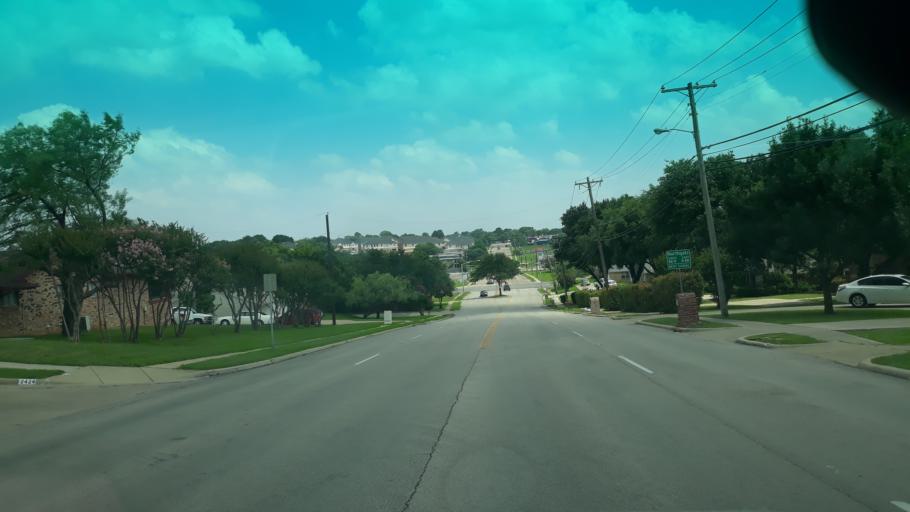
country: US
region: Texas
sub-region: Dallas County
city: Irving
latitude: 32.8569
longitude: -96.9800
